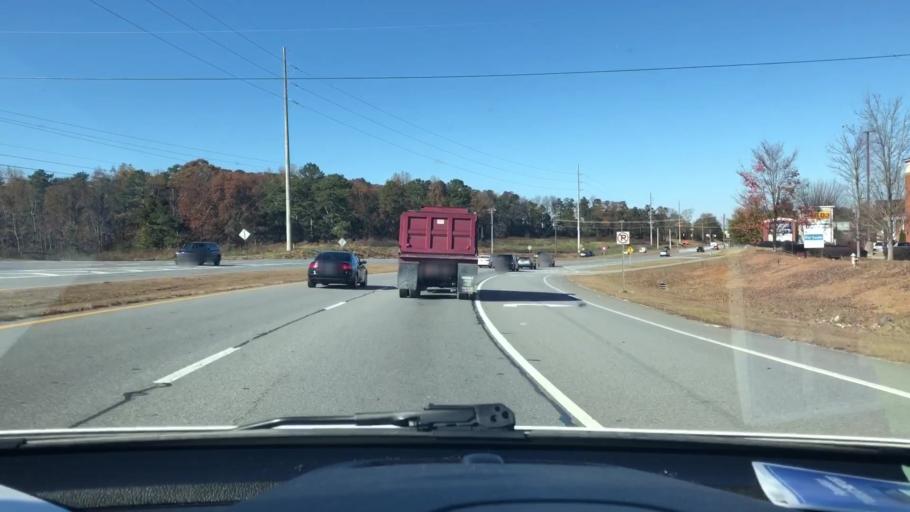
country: US
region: Georgia
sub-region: Fulton County
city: Johns Creek
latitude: 34.0965
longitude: -84.1770
